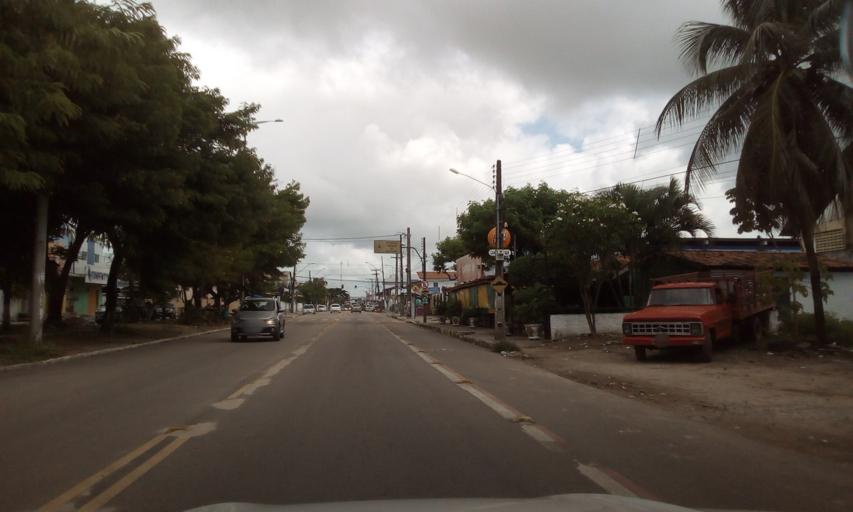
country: BR
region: Paraiba
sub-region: Conde
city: Conde
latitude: -7.1990
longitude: -34.8495
